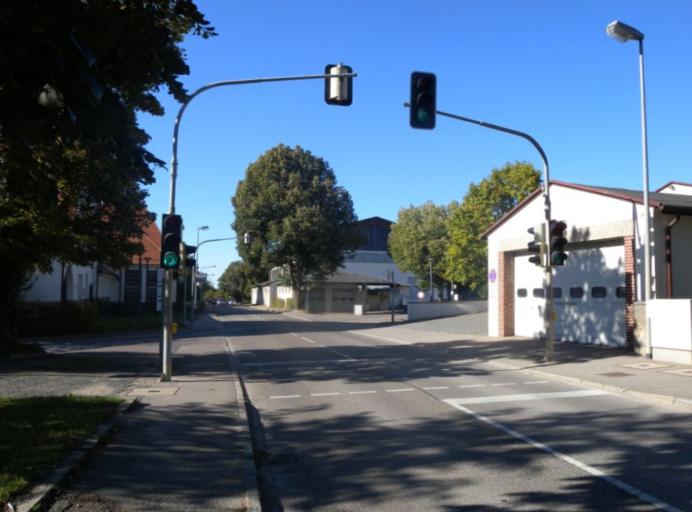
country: DE
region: Baden-Wuerttemberg
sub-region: Tuebingen Region
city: Grabenstetten
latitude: 48.5553
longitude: 9.4687
